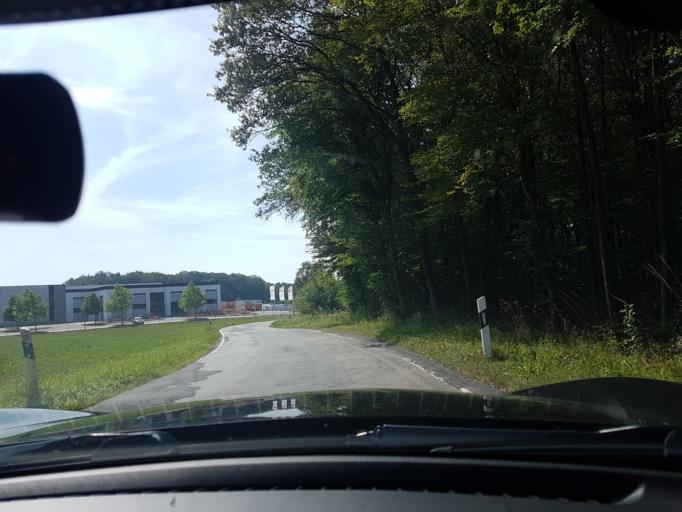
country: DE
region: Baden-Wuerttemberg
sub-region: Karlsruhe Region
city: Limbach
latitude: 49.4621
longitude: 9.2514
